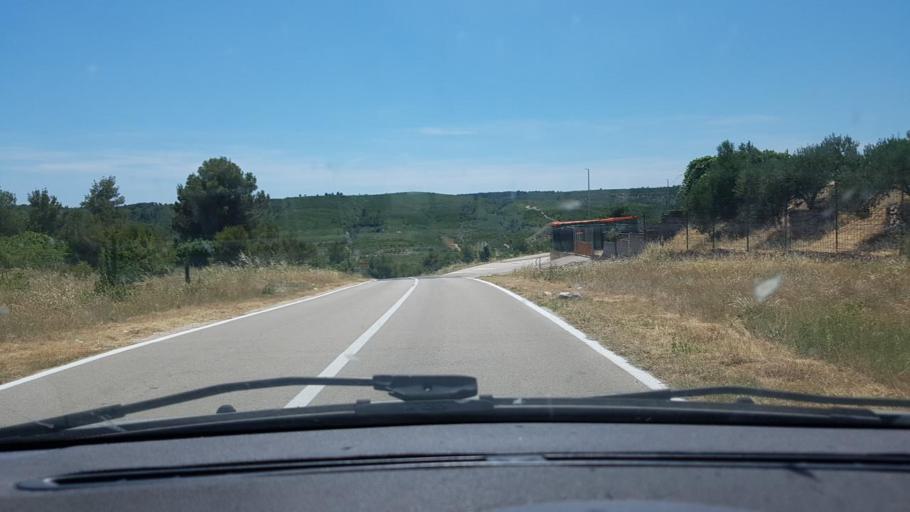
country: HR
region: Sibensko-Kniniska
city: Kistanje
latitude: 43.9083
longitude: 15.9251
